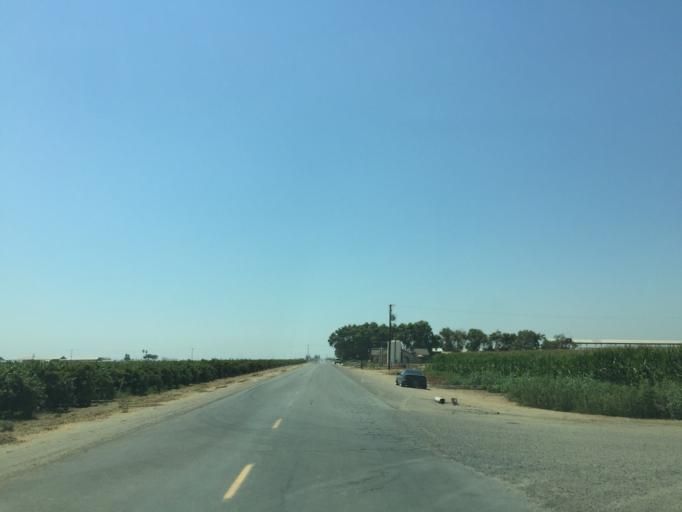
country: US
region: California
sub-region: Tulare County
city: Goshen
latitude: 36.3710
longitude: -119.3631
